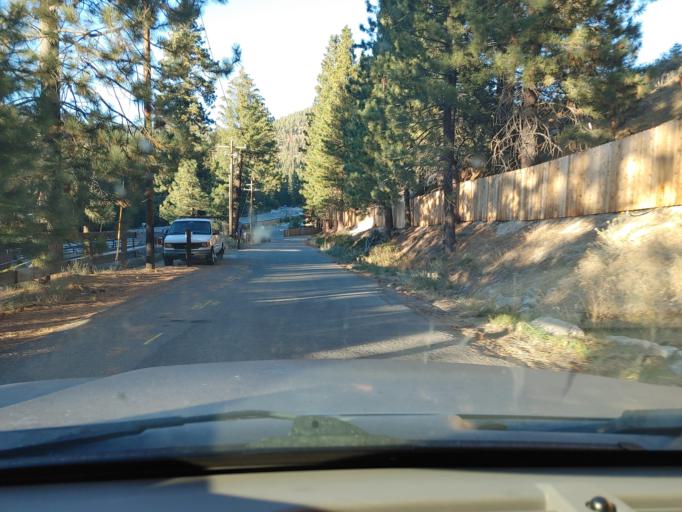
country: US
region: Nevada
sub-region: Washoe County
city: Incline Village
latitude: 39.2339
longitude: -119.9300
